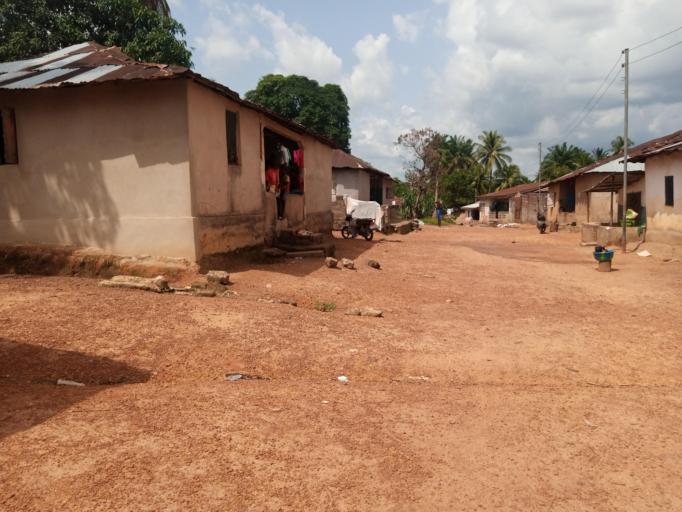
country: SL
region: Southern Province
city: Bo
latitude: 7.9751
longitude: -11.7339
